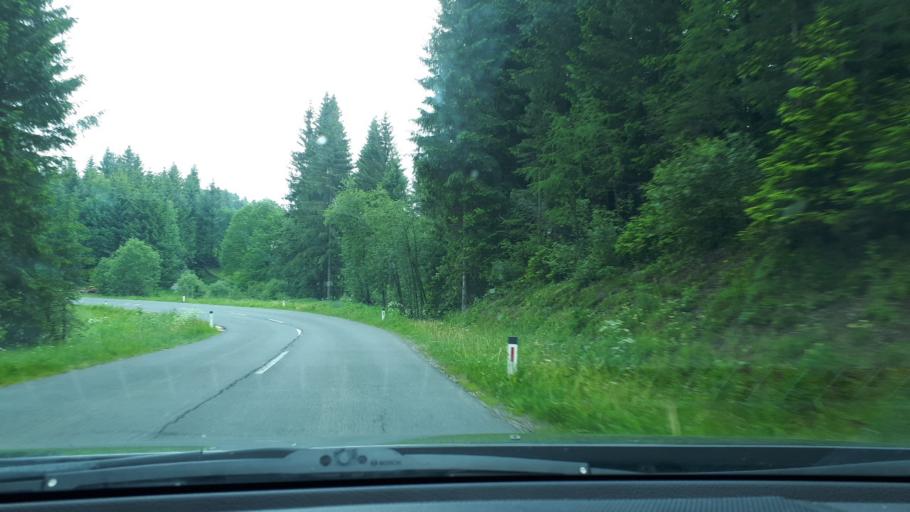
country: AT
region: Carinthia
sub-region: Politischer Bezirk Wolfsberg
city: Preitenegg
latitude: 46.9345
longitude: 14.9671
